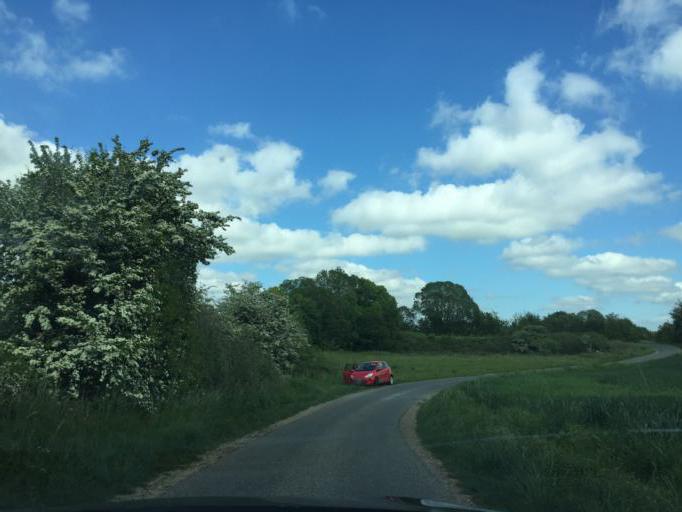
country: DK
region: South Denmark
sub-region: Assens Kommune
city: Tommerup
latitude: 55.3449
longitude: 10.2183
